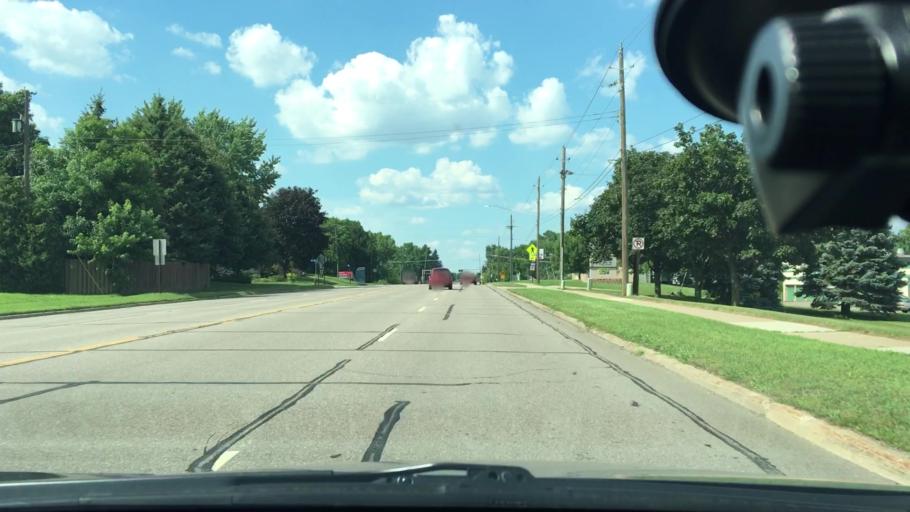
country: US
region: Minnesota
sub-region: Hennepin County
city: New Hope
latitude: 45.0461
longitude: -93.3803
